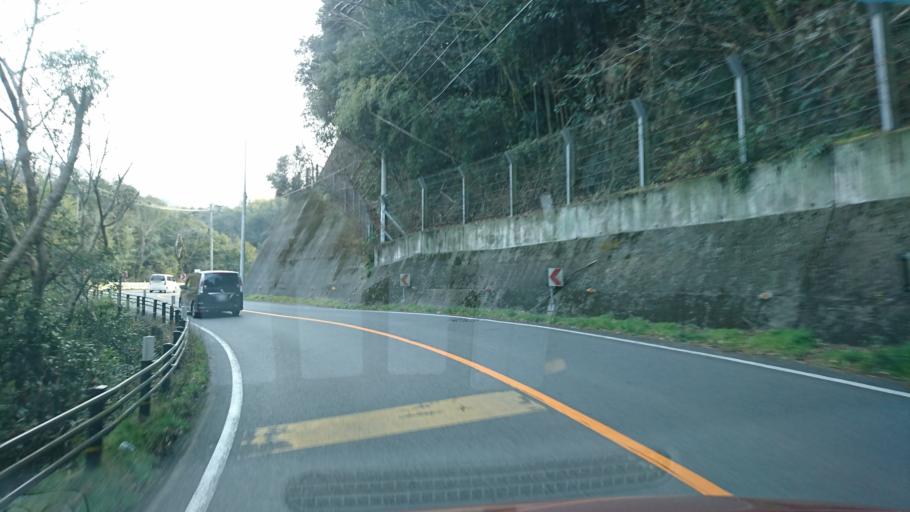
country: JP
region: Ehime
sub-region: Shikoku-chuo Shi
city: Matsuyama
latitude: 33.8917
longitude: 132.8390
